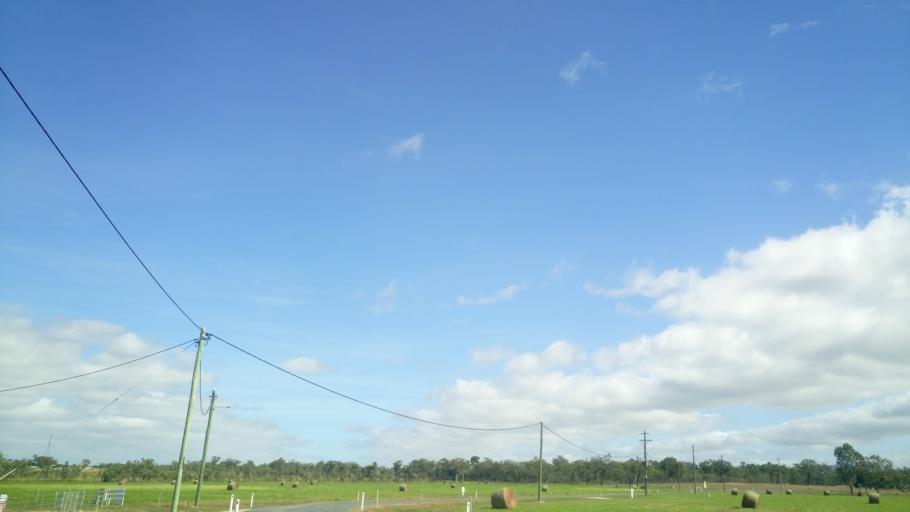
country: AU
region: Queensland
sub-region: Tablelands
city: Mareeba
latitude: -16.9962
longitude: 145.3950
